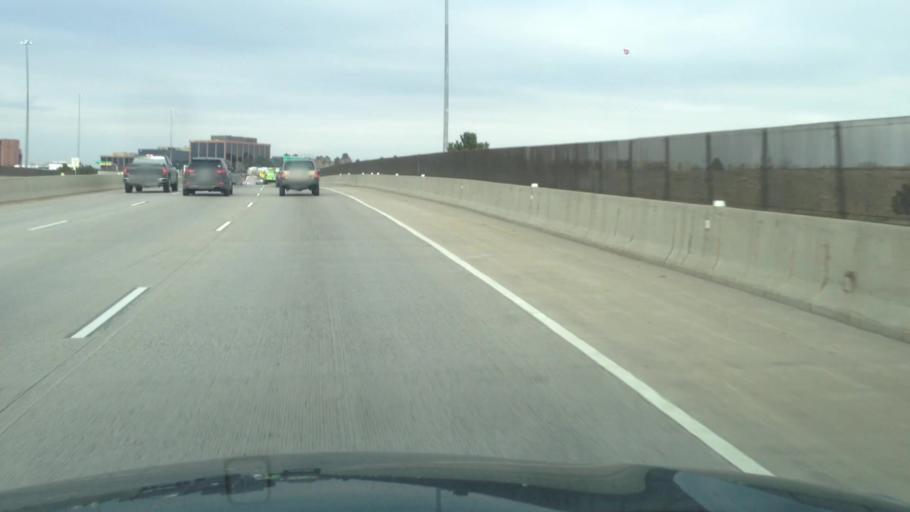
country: US
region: Colorado
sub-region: Arapahoe County
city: Dove Valley
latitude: 39.6519
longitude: -104.8318
